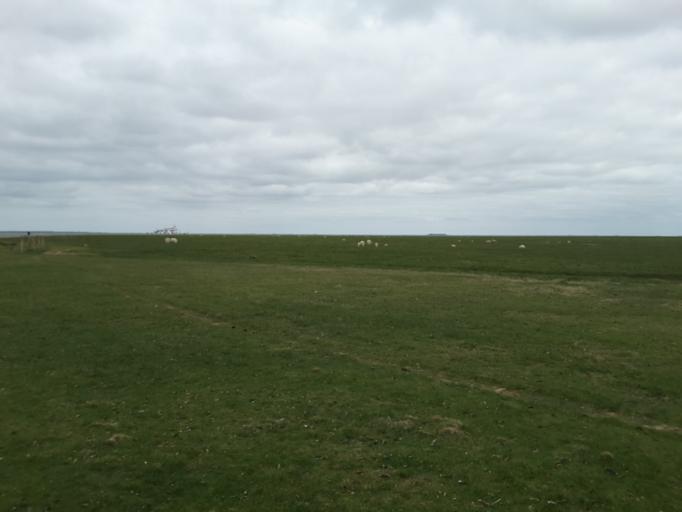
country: DE
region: Schleswig-Holstein
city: Grode
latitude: 54.6300
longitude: 8.7147
